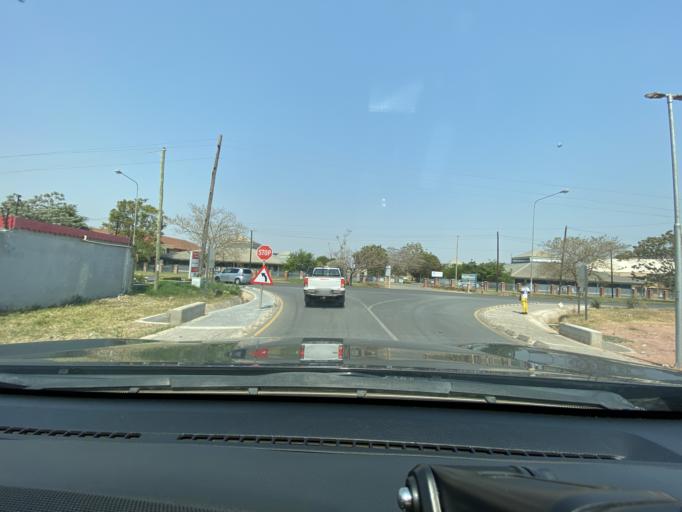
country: ZM
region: Lusaka
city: Lusaka
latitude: -15.3931
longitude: 28.3215
